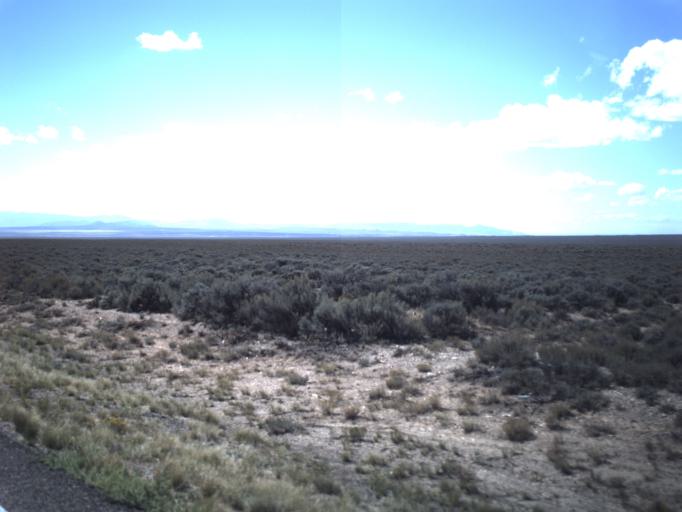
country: US
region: Utah
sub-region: Iron County
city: Enoch
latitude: 37.9850
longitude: -113.0024
